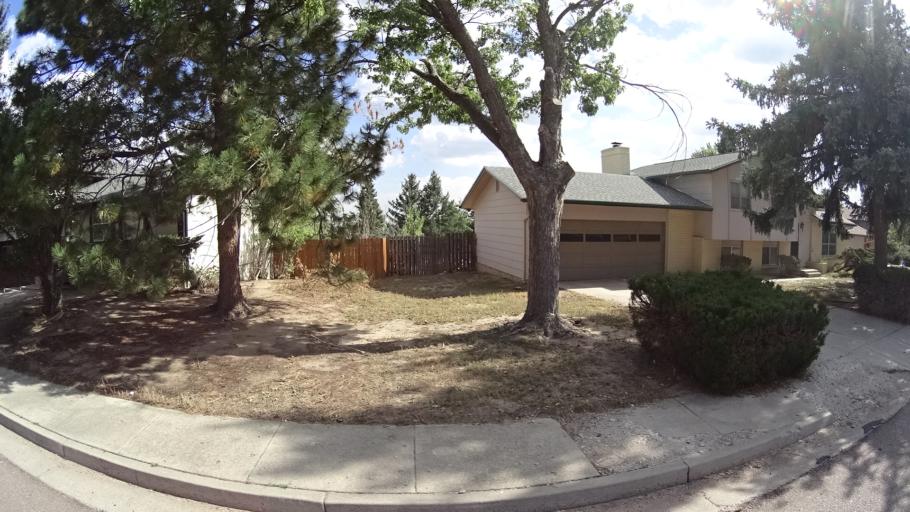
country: US
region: Colorado
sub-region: El Paso County
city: Cimarron Hills
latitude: 38.8704
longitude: -104.7337
